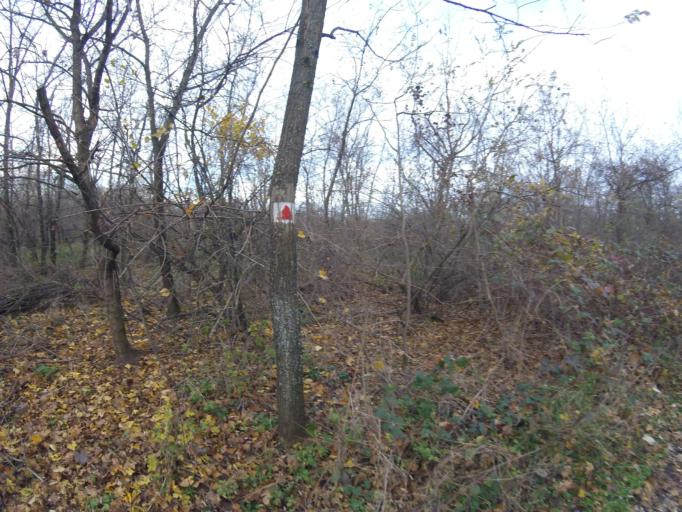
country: HU
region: Heves
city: Abasar
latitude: 47.8220
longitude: 19.9988
